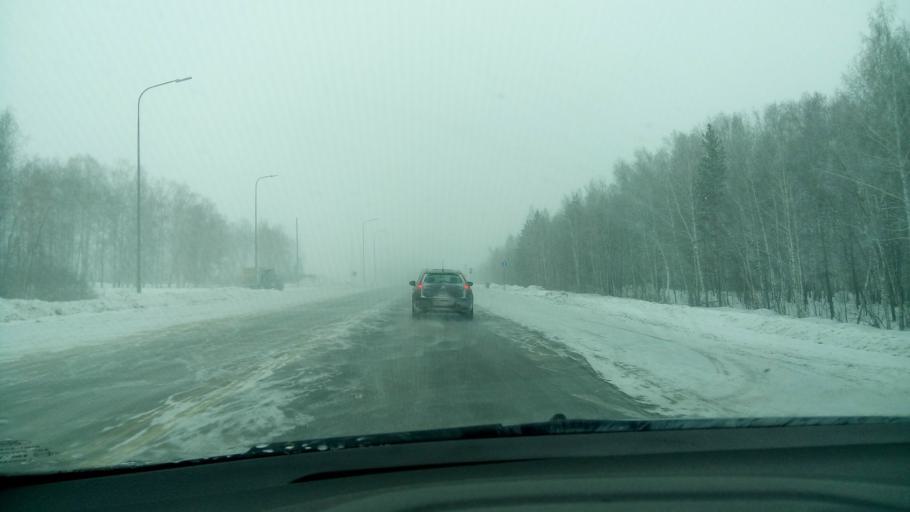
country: RU
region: Sverdlovsk
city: Bogdanovich
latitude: 56.7756
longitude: 61.9860
